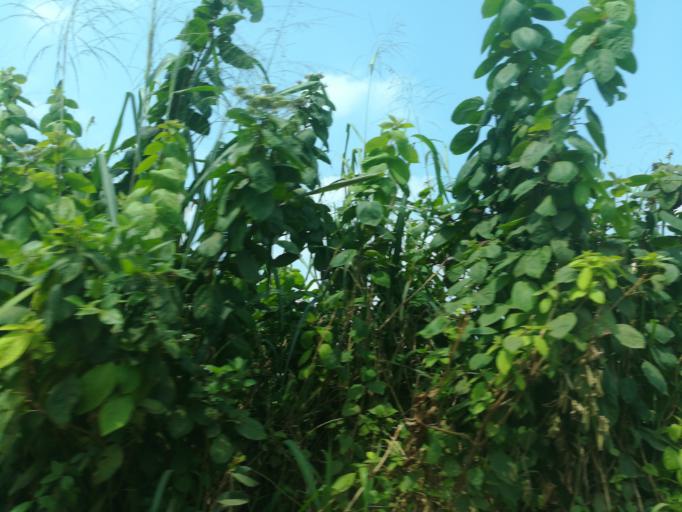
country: NG
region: Lagos
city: Ikorodu
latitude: 6.5982
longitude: 3.6304
